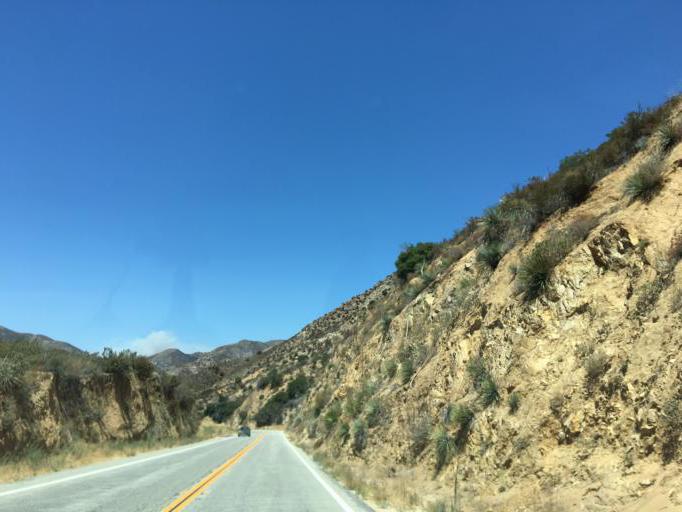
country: US
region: California
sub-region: Los Angeles County
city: La Crescenta-Montrose
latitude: 34.2951
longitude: -118.2375
